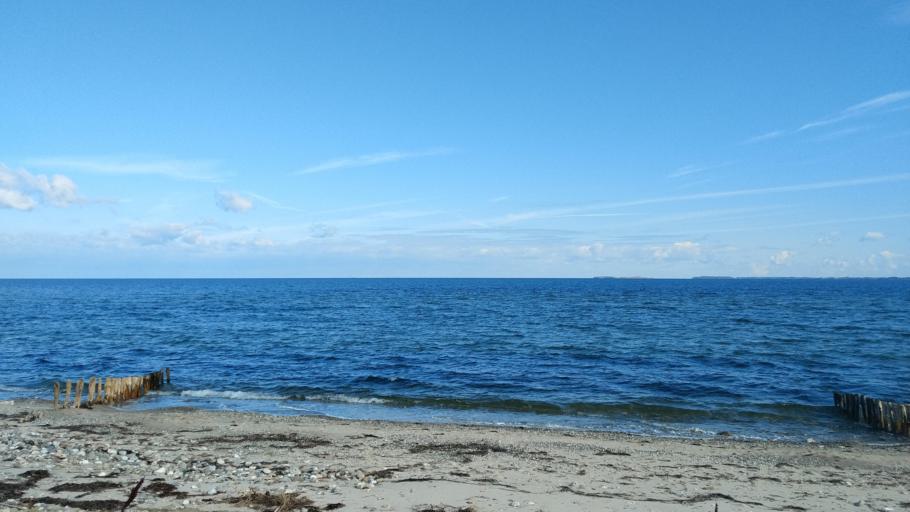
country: DK
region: South Denmark
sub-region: Kerteminde Kommune
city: Munkebo
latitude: 55.5446
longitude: 10.5082
